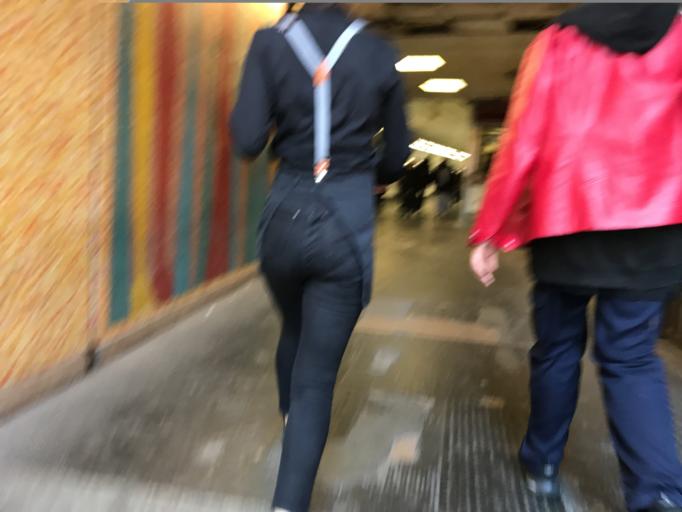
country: VA
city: Vatican City
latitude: 41.9064
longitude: 12.4828
